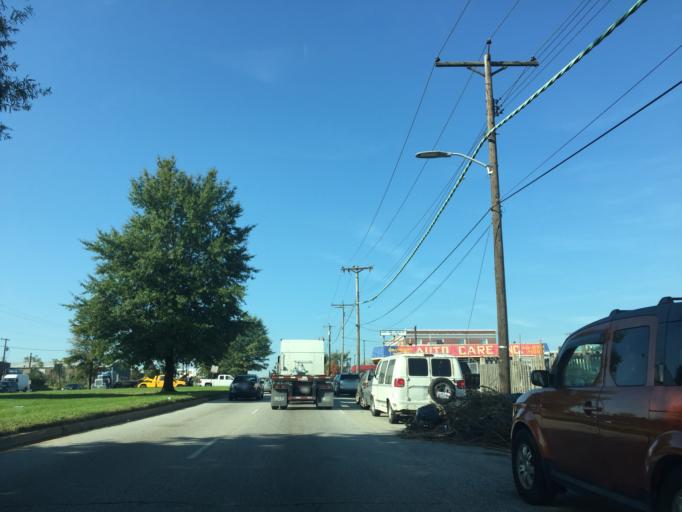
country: US
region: Maryland
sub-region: Baltimore County
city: Rosedale
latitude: 39.3013
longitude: -76.5439
